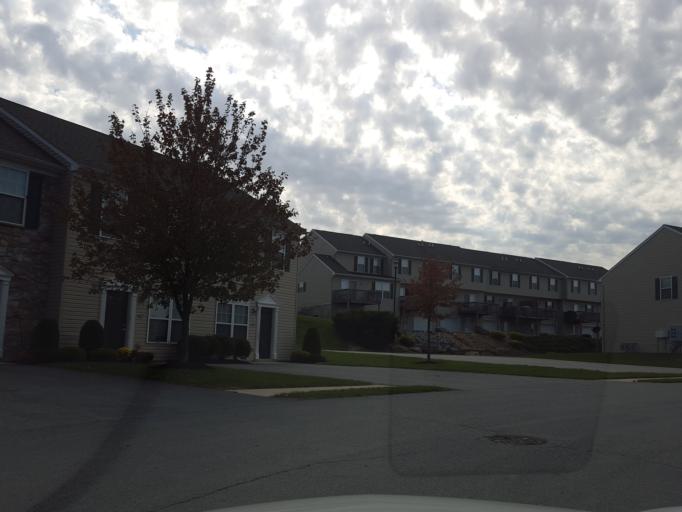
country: US
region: Pennsylvania
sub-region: York County
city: Yoe
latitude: 39.9204
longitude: -76.6263
